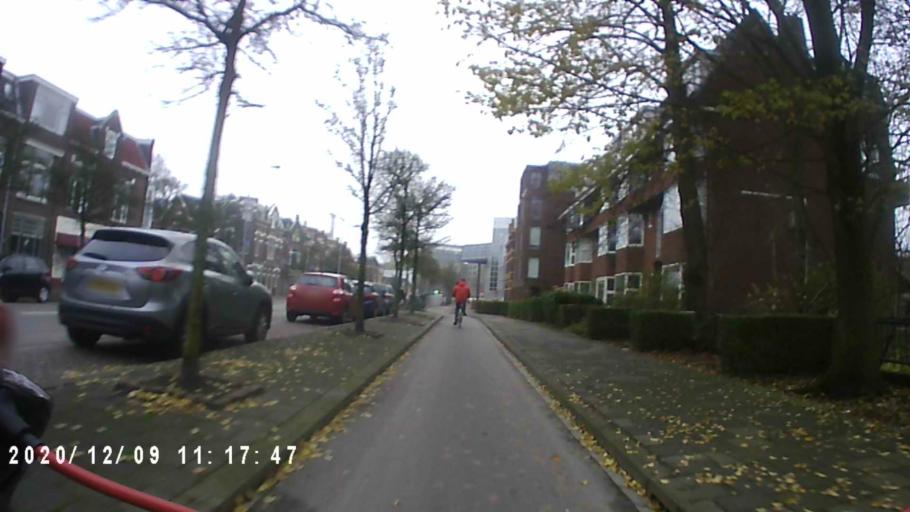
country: NL
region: Groningen
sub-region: Gemeente Groningen
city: Groningen
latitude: 53.2160
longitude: 6.5480
